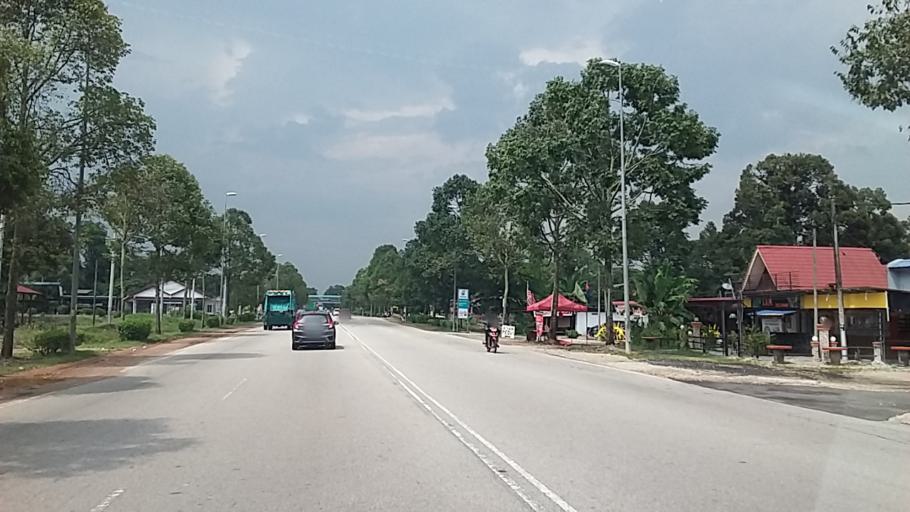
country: MY
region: Johor
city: Parit Raja
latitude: 1.8695
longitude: 103.1248
